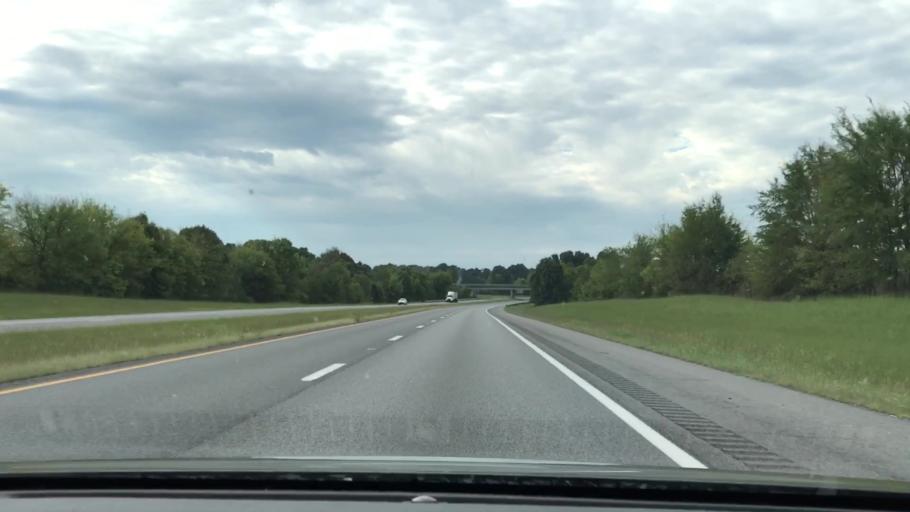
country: US
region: Kentucky
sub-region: Marshall County
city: Benton
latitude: 36.9053
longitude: -88.3481
